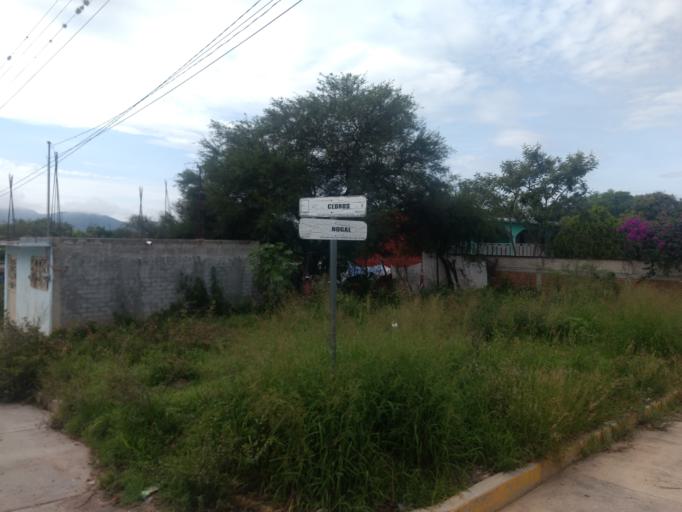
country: MX
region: Oaxaca
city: Ciudad de Huajuapam de Leon
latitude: 17.8049
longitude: -97.7914
